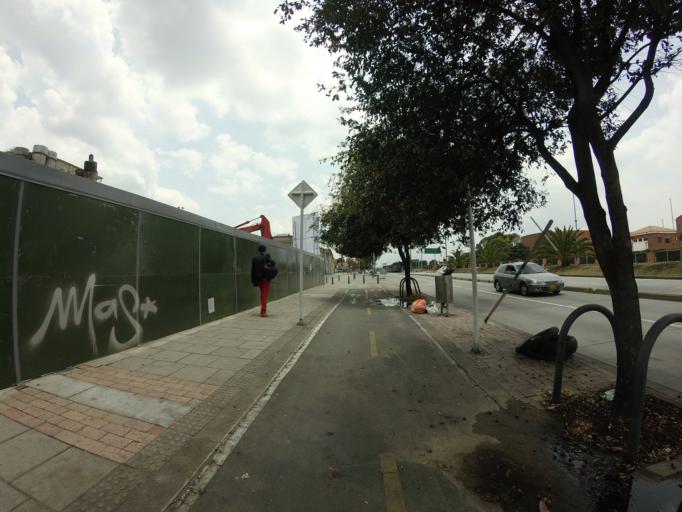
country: CO
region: Bogota D.C.
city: Barrio San Luis
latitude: 4.6774
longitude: -74.0664
